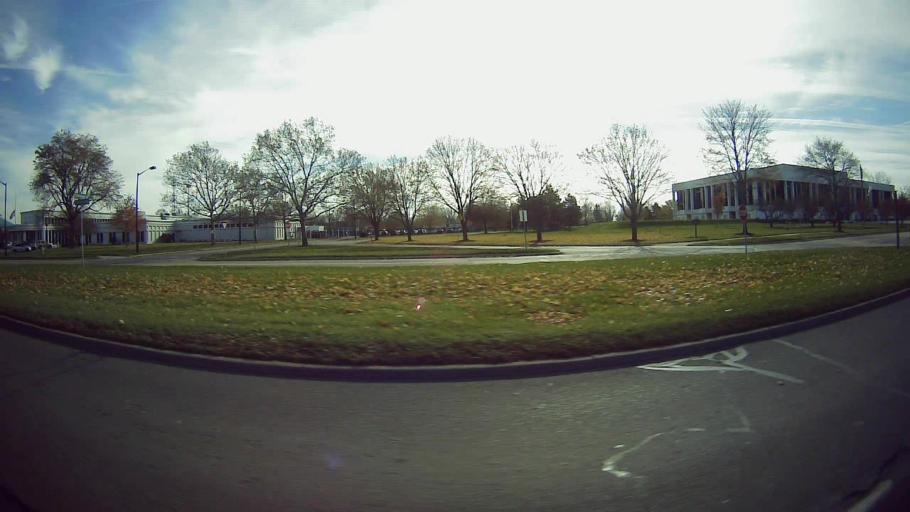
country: US
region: Michigan
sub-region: Wayne County
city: Dearborn
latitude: 42.3138
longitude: -83.2035
